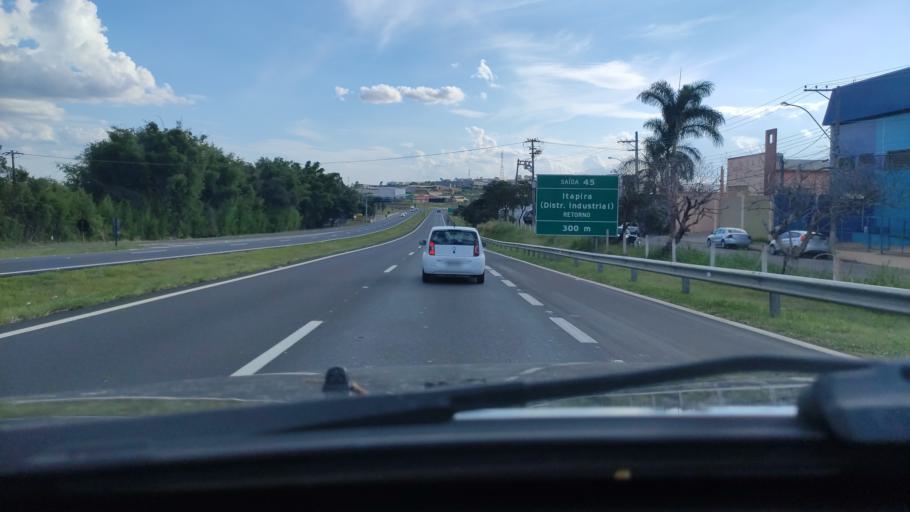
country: BR
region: Sao Paulo
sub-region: Itapira
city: Itapira
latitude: -22.4478
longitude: -46.8349
